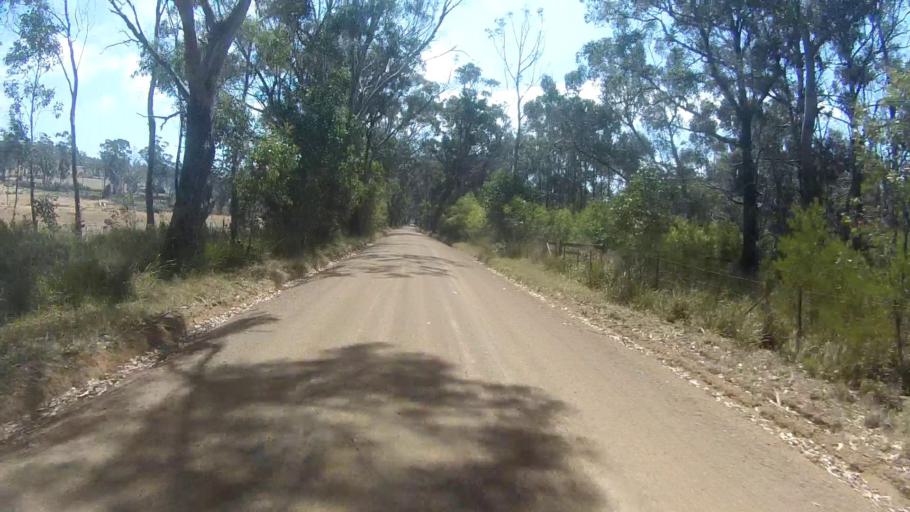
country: AU
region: Tasmania
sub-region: Sorell
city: Sorell
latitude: -42.8551
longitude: 147.8329
